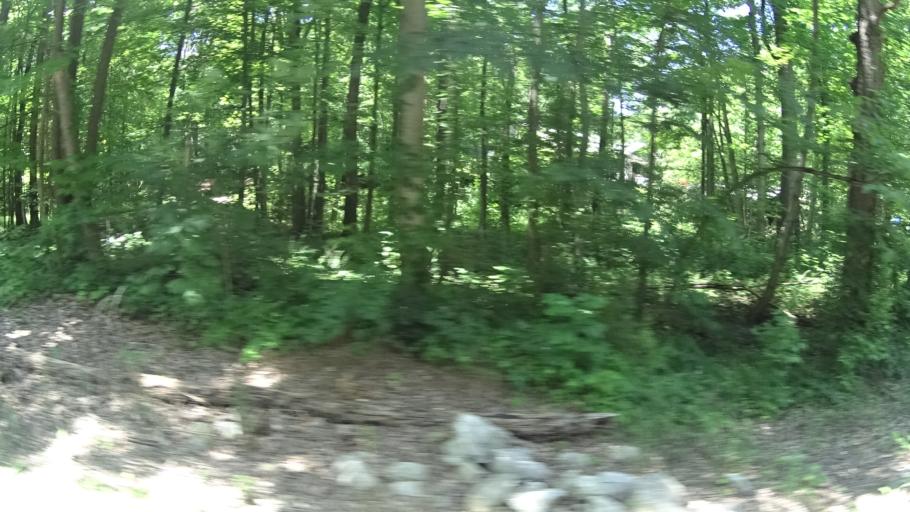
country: US
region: Ohio
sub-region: Lorain County
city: Vermilion
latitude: 41.3516
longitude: -82.3973
